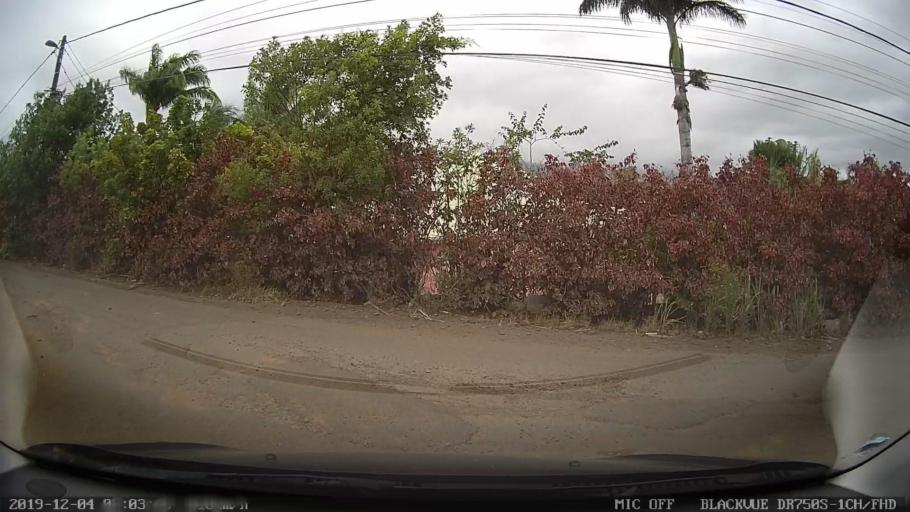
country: RE
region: Reunion
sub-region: Reunion
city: Sainte-Marie
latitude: -20.9218
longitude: 55.5254
